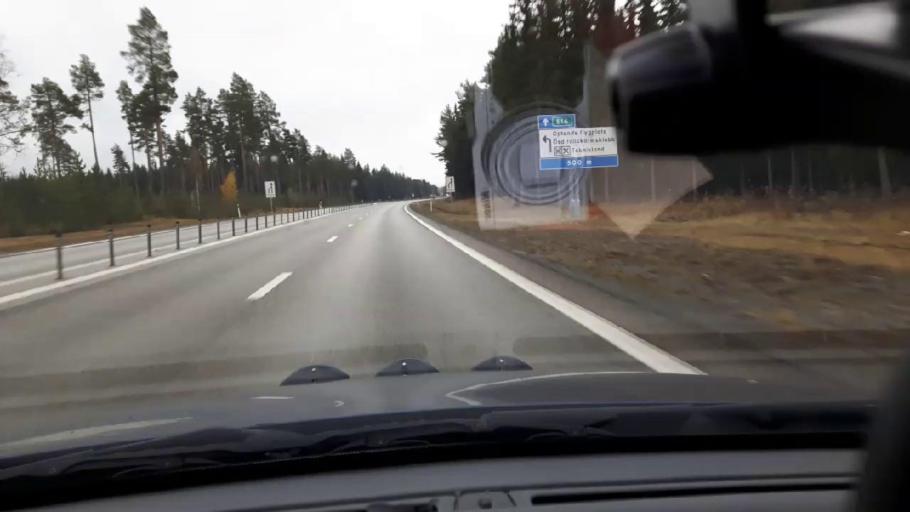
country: SE
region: Jaemtland
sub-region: OEstersunds Kommun
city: Brunflo
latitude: 63.1320
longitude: 14.7904
